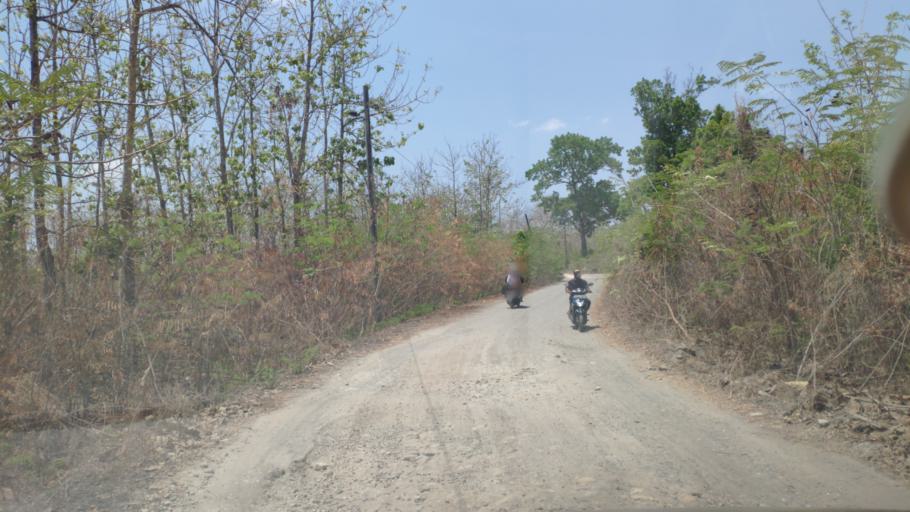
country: ID
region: Central Java
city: Randublatung
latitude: -7.2525
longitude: 111.3796
